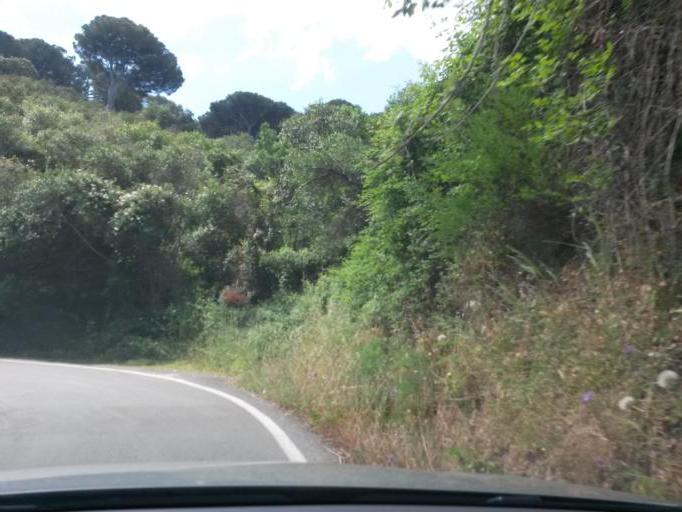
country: IT
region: Tuscany
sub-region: Provincia di Livorno
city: Porto Azzurro
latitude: 42.7563
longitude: 10.3920
